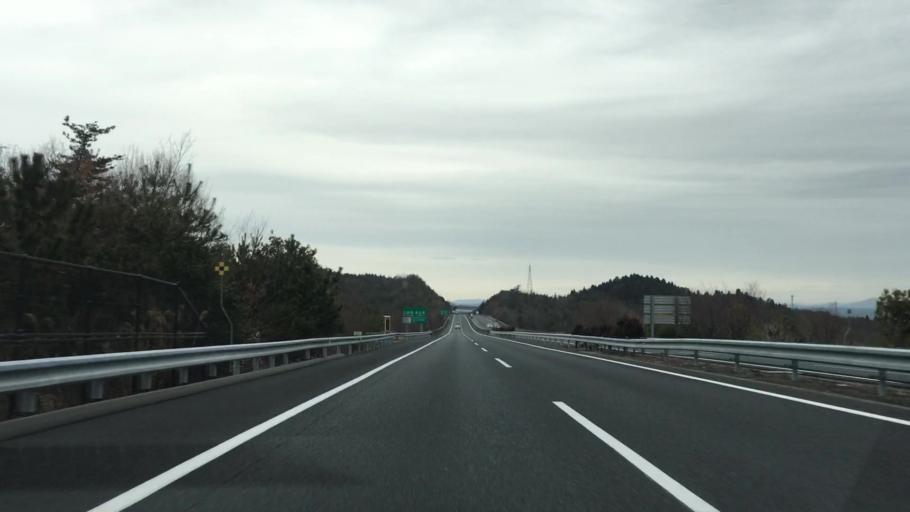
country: JP
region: Gifu
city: Toki
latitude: 35.3202
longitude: 137.1763
